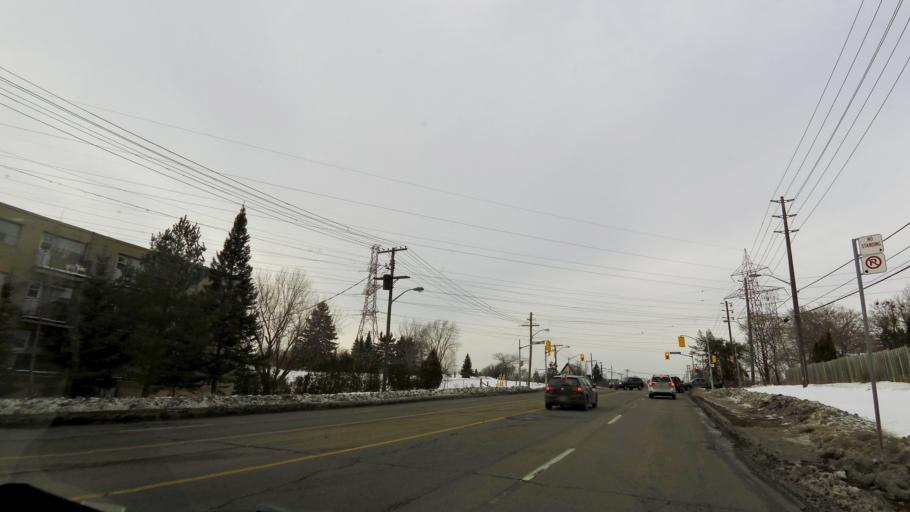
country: CA
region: Ontario
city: Etobicoke
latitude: 43.7209
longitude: -79.5578
